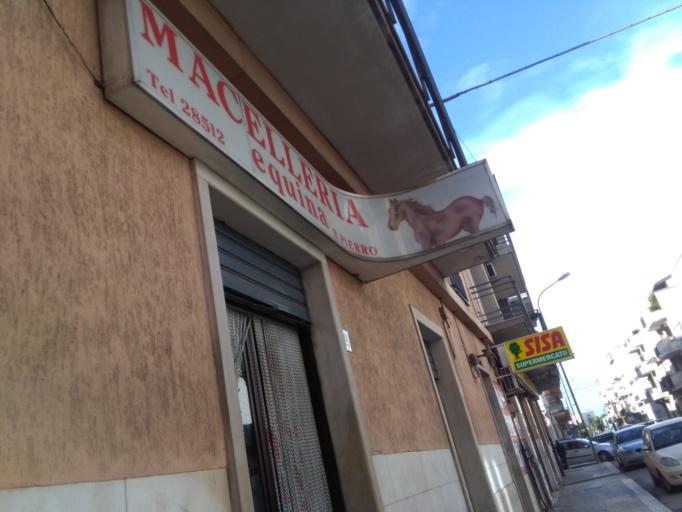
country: IT
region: Apulia
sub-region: Provincia di Barletta - Andria - Trani
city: Andria
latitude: 41.2328
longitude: 16.2937
